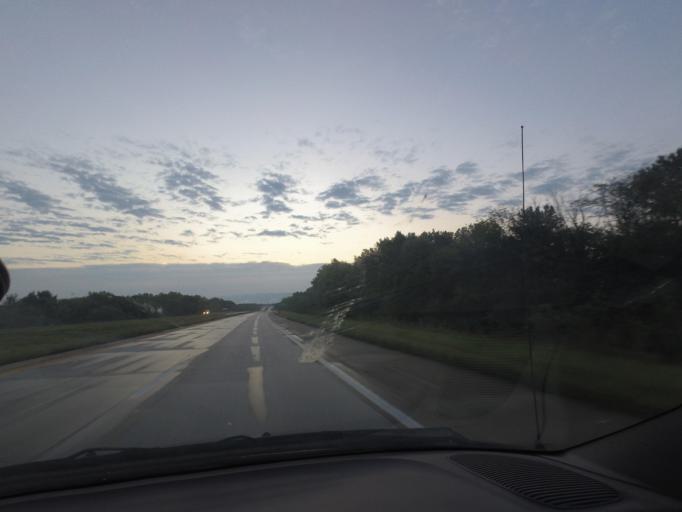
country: US
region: Missouri
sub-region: Macon County
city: Macon
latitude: 39.7584
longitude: -92.6001
